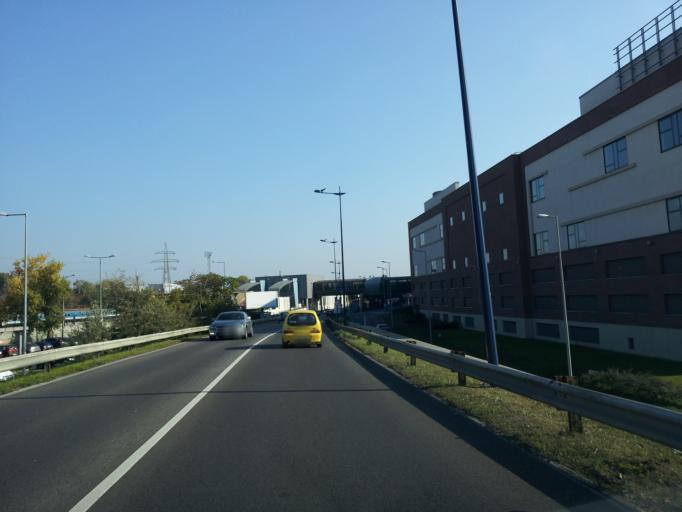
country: HU
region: Budapest
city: Budapest XIX. keruelet
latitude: 47.4639
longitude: 19.1450
